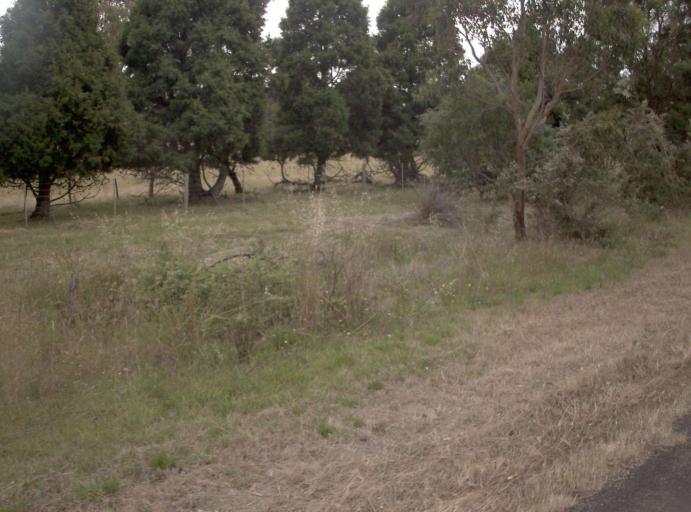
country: AU
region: Victoria
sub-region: Wellington
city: Sale
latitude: -38.3758
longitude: 146.9836
